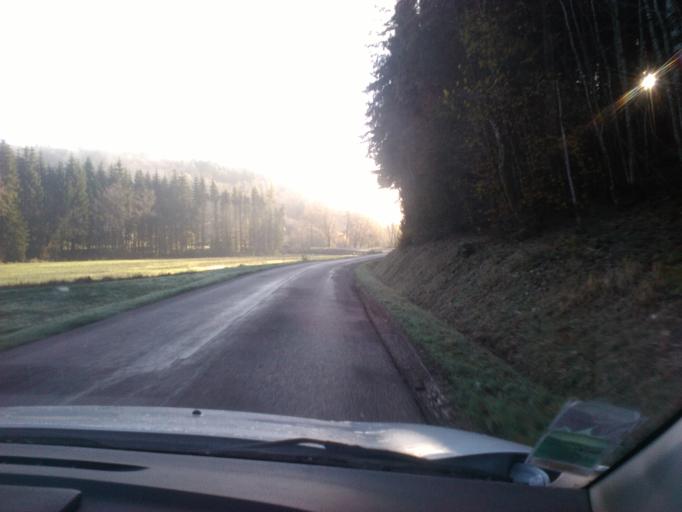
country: FR
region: Lorraine
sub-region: Departement des Vosges
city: Uzemain
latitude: 48.0704
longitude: 6.3114
